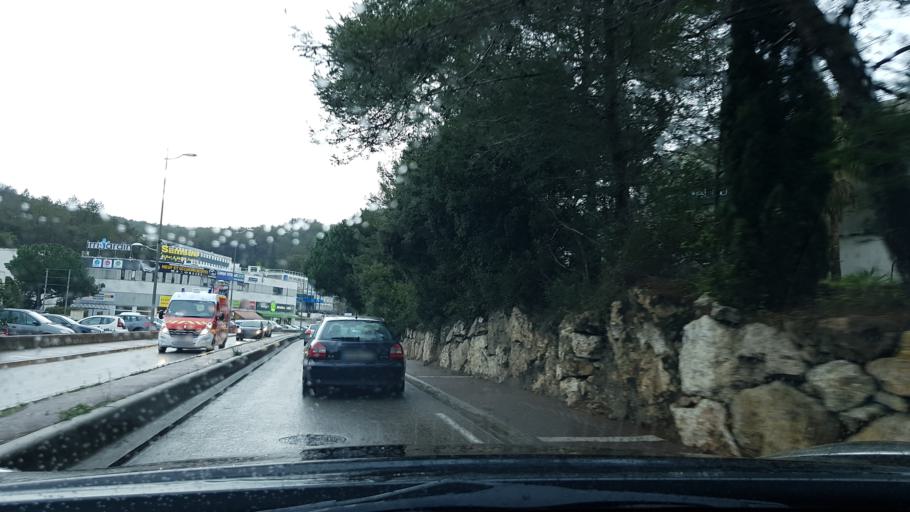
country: FR
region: Provence-Alpes-Cote d'Azur
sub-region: Departement des Alpes-Maritimes
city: Vallauris
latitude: 43.6021
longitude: 7.0611
